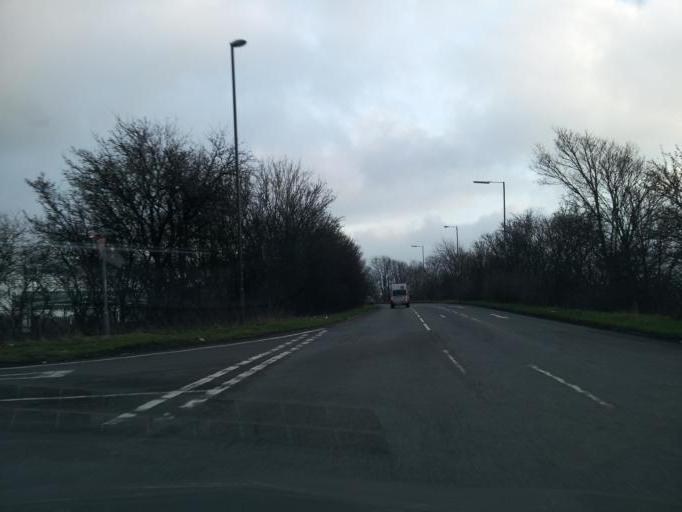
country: GB
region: England
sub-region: Derbyshire
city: Etwall
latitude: 52.8550
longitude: -1.5862
